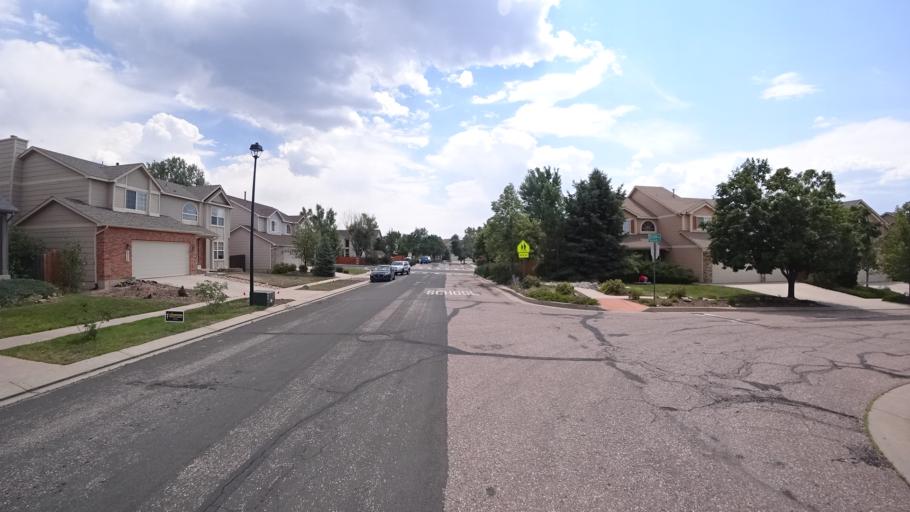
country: US
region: Colorado
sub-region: El Paso County
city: Black Forest
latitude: 38.9632
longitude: -104.7702
